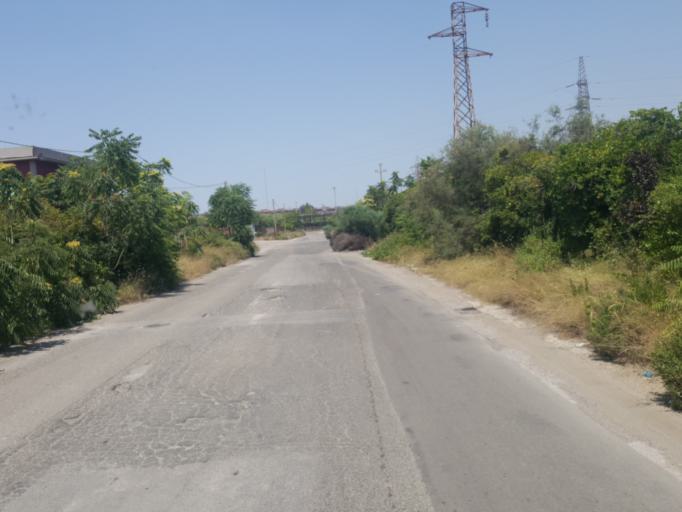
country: IT
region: Apulia
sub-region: Provincia di Taranto
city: Statte
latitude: 40.4999
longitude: 17.1986
